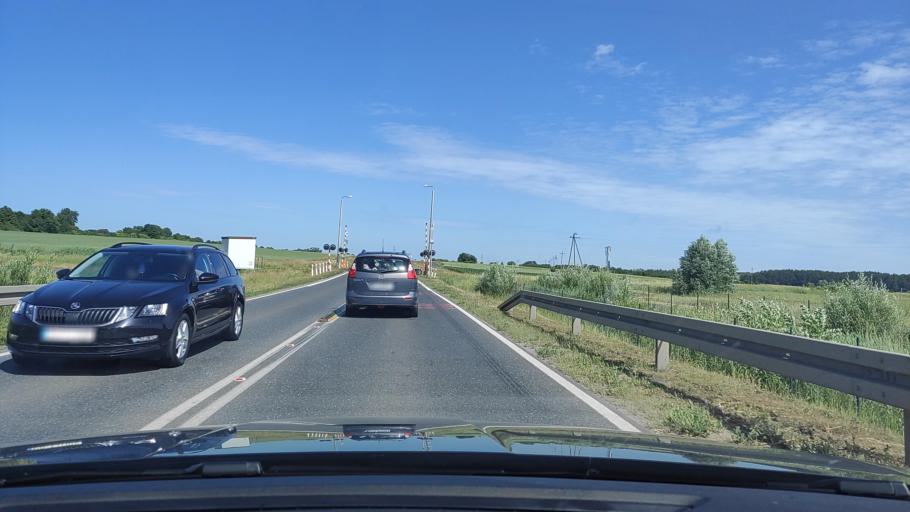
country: PL
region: Greater Poland Voivodeship
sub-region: Powiat poznanski
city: Murowana Goslina
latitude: 52.5522
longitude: 16.9905
